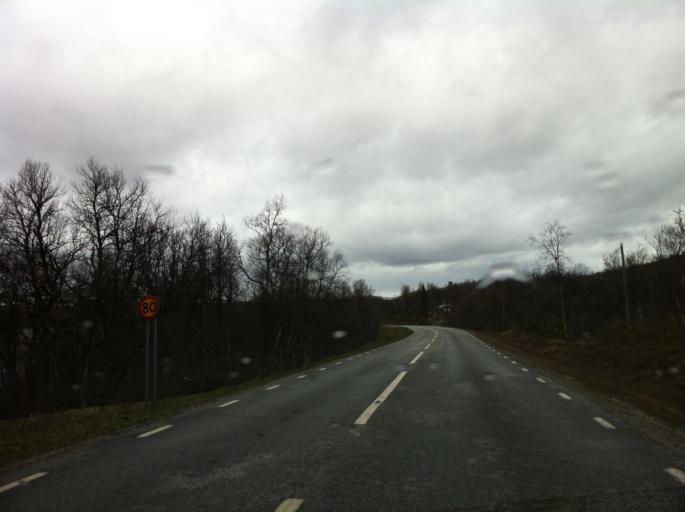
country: NO
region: Sor-Trondelag
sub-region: Tydal
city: Aas
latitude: 62.6063
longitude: 12.1641
